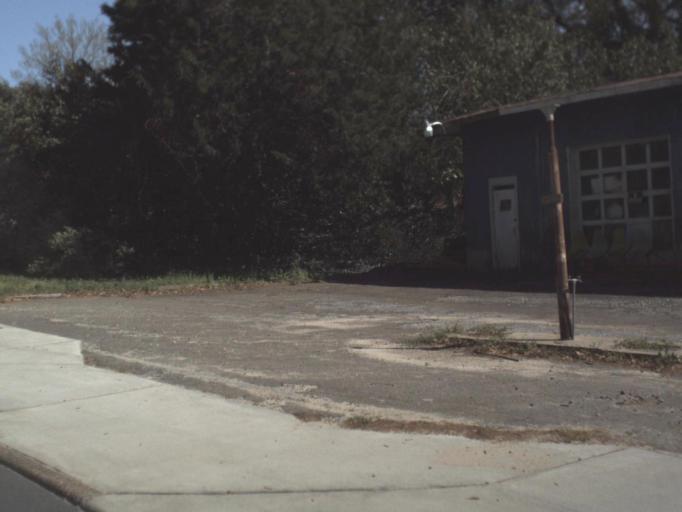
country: US
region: Florida
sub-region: Walton County
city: DeFuniak Springs
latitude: 30.7208
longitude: -86.1076
